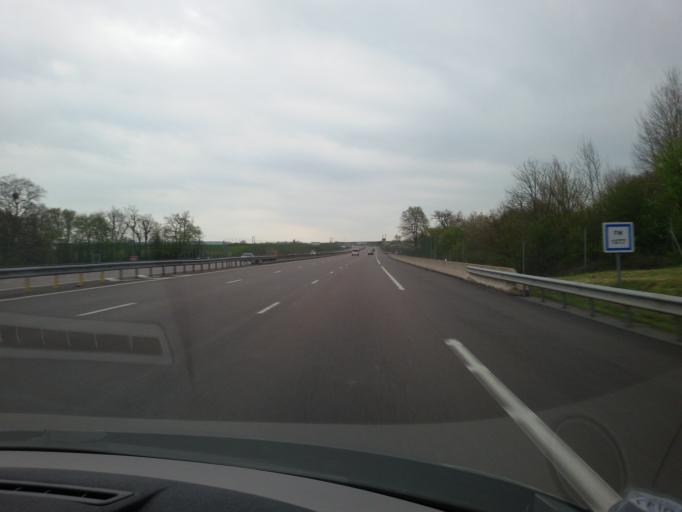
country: FR
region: Champagne-Ardenne
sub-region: Departement de la Haute-Marne
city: Langres
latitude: 47.8311
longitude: 5.2281
